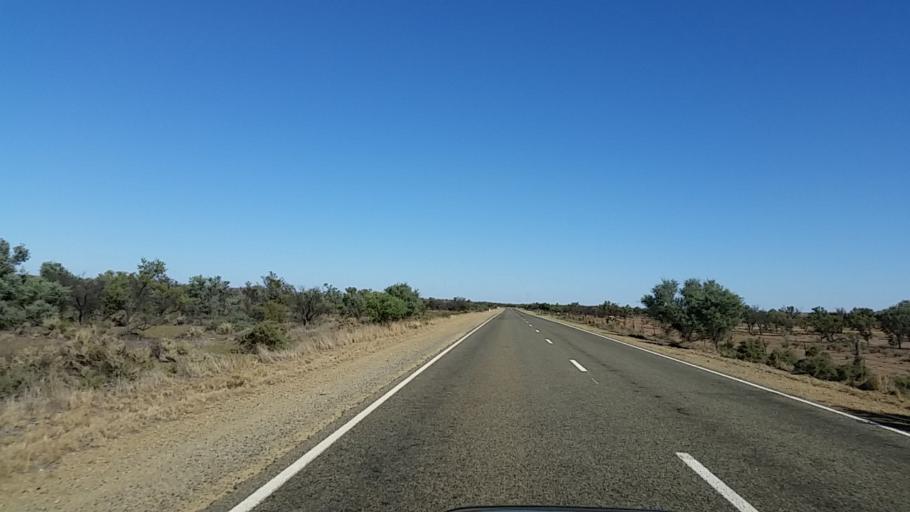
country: AU
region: South Australia
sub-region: Flinders Ranges
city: Quorn
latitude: -32.3822
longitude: 138.5015
